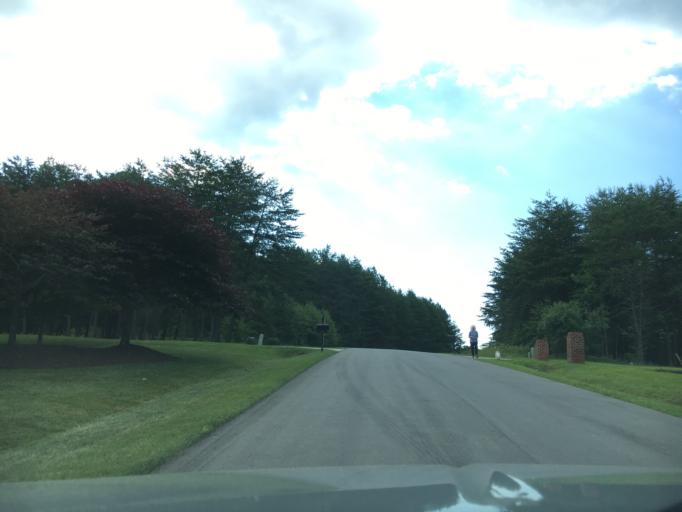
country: US
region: Virginia
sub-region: Bedford County
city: Forest
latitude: 37.3878
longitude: -79.2669
